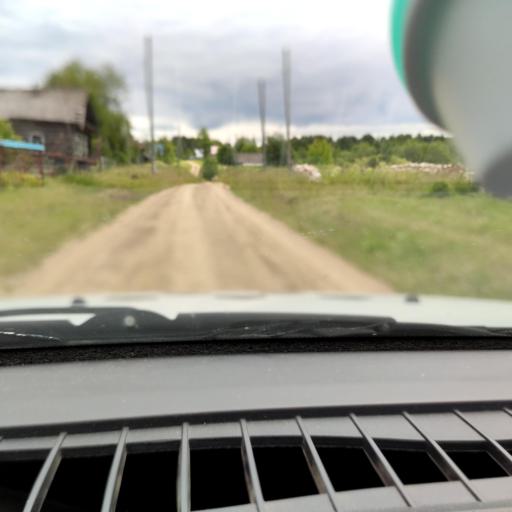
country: RU
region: Perm
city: Suksun
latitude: 57.2109
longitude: 57.7010
